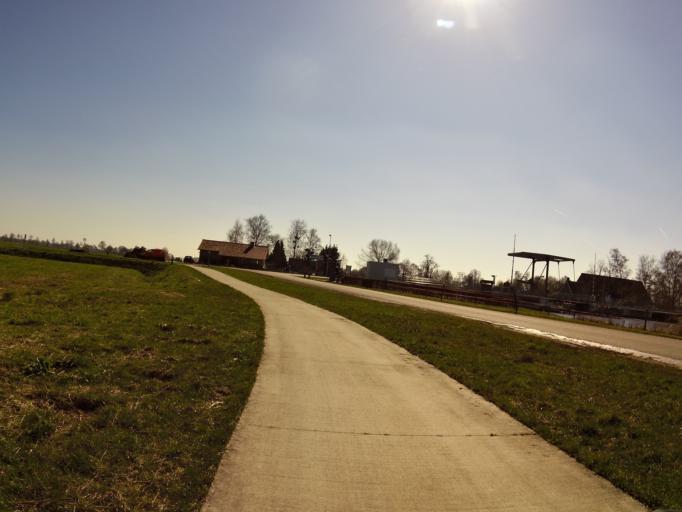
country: NL
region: Overijssel
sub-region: Gemeente Steenwijkerland
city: Blokzijl
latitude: 52.7557
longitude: 5.9961
